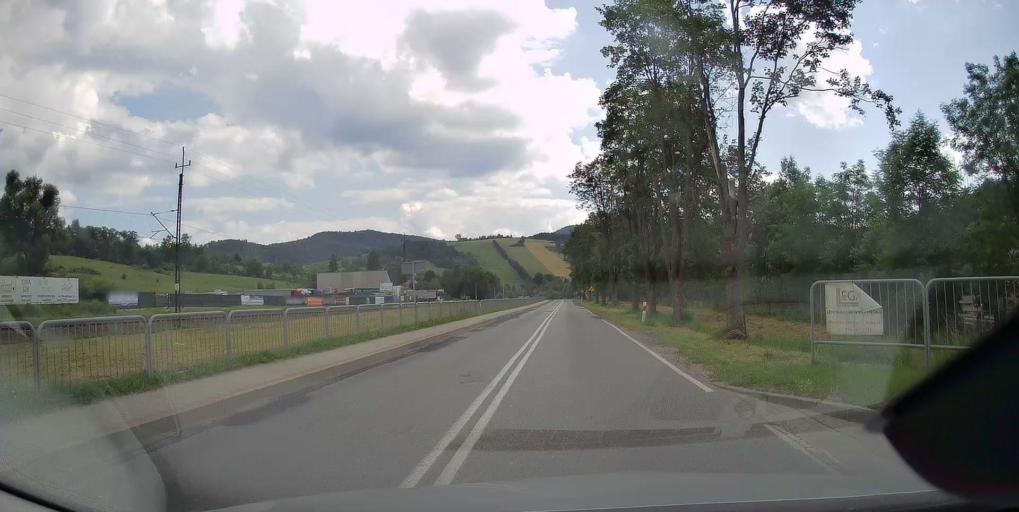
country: PL
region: Lesser Poland Voivodeship
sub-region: Powiat nowosadecki
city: Krynica-Zdroj
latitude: 49.3766
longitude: 20.9505
